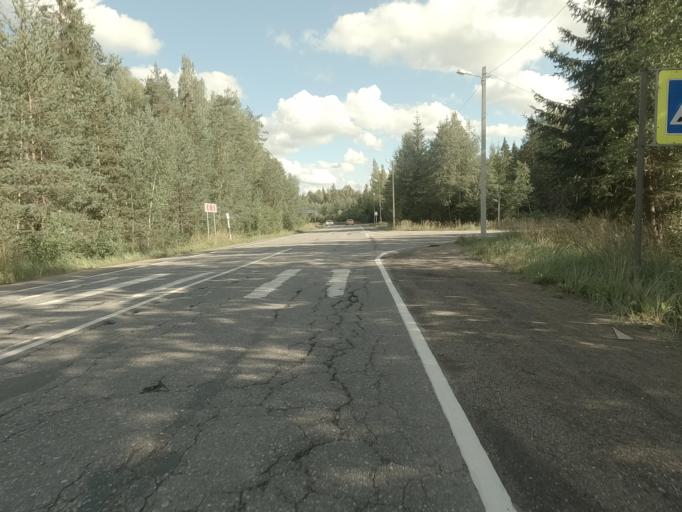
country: RU
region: Leningrad
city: Borisova Griva
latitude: 59.9869
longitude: 30.8885
